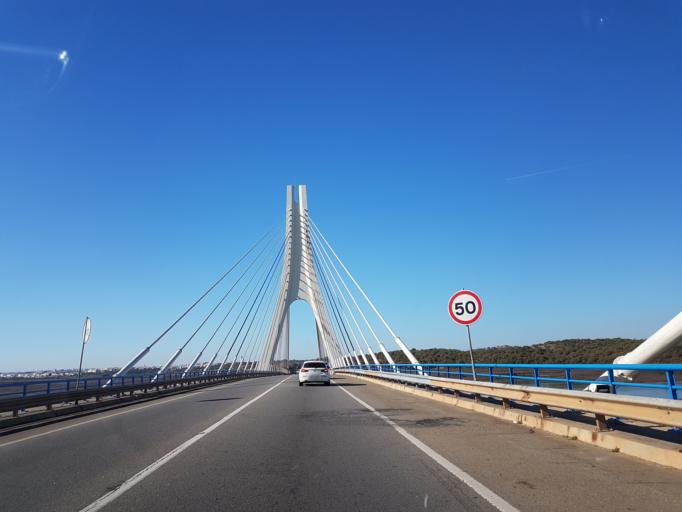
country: PT
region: Faro
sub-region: Lagoa
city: Estombar
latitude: 37.1515
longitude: -8.5064
